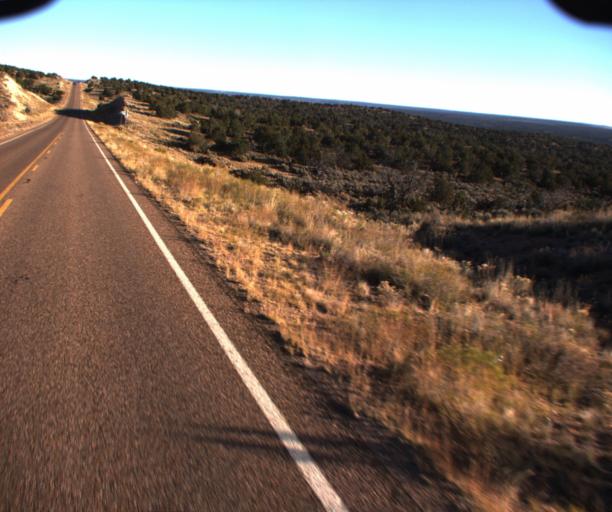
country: US
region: Arizona
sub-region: Apache County
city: Ganado
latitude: 35.4755
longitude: -109.5296
